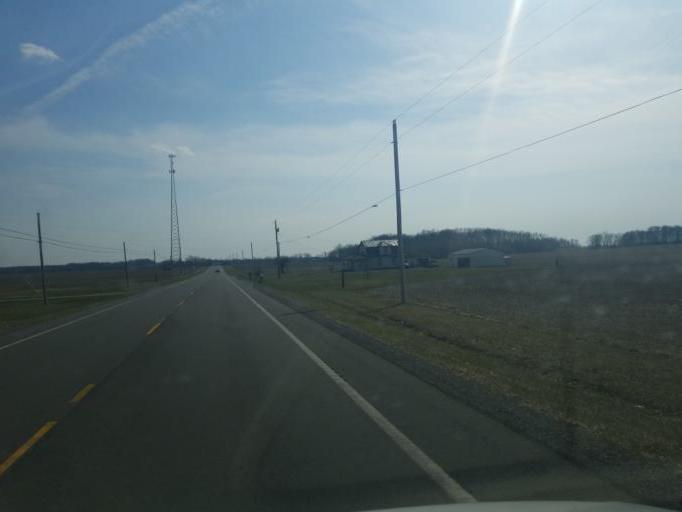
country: US
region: Ohio
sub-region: Logan County
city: Northwood
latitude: 40.5165
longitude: -83.6884
